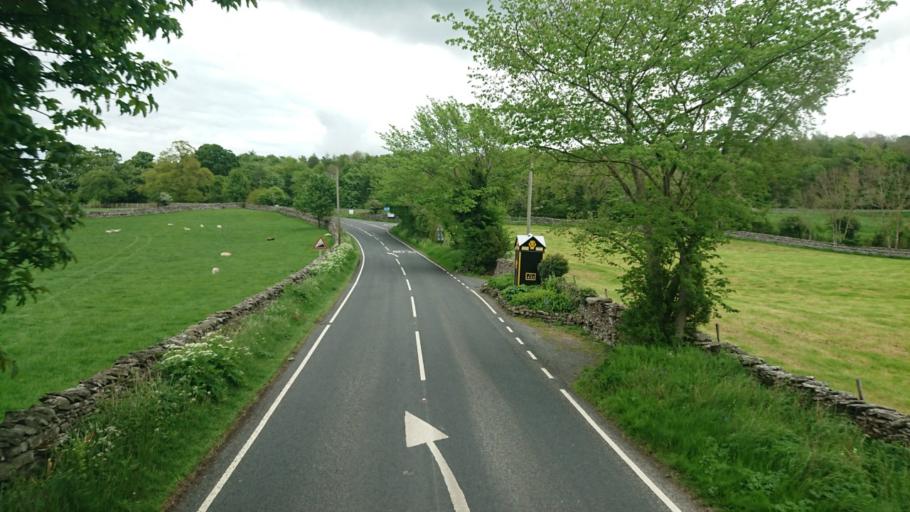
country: GB
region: England
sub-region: North Yorkshire
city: Leyburn
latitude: 54.2956
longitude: -1.9608
